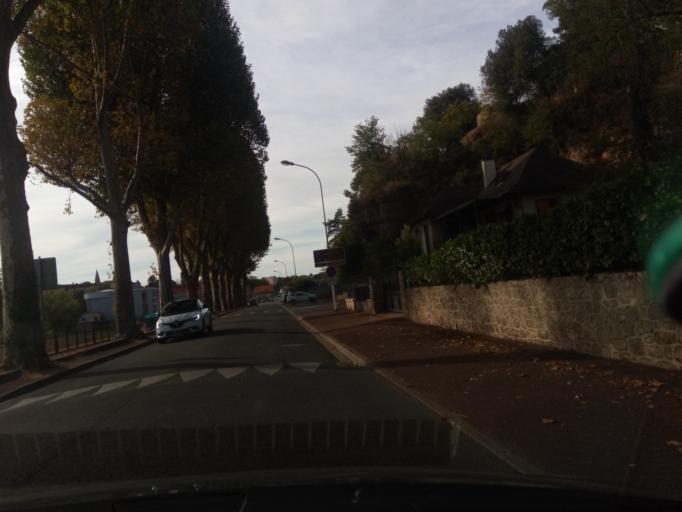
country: FR
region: Poitou-Charentes
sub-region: Departement de la Vienne
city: Montmorillon
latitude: 46.4207
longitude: 0.8742
